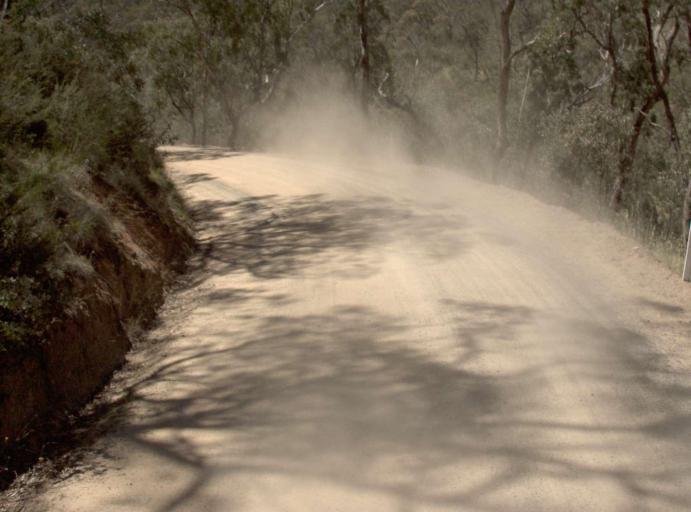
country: AU
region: New South Wales
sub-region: Snowy River
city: Jindabyne
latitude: -37.0379
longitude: 148.5553
